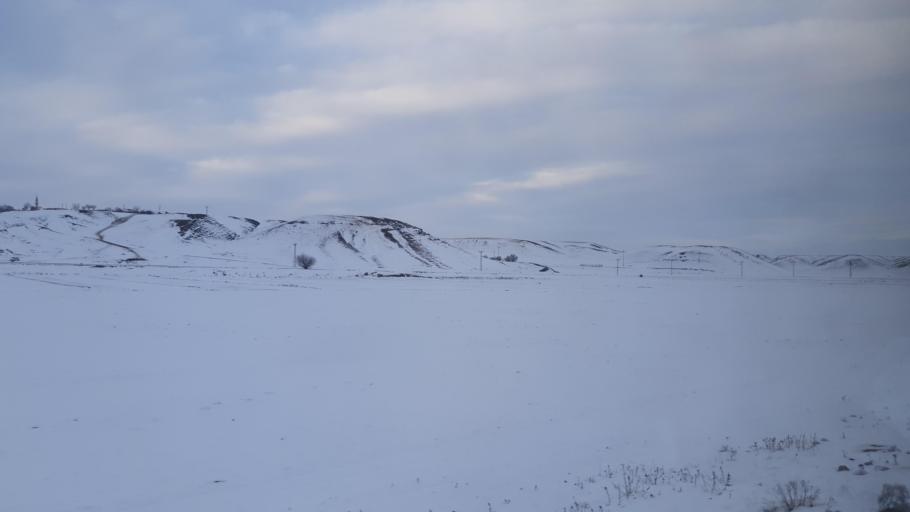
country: TR
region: Kirsehir
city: Mecidiye
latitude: 39.6868
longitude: 34.3926
